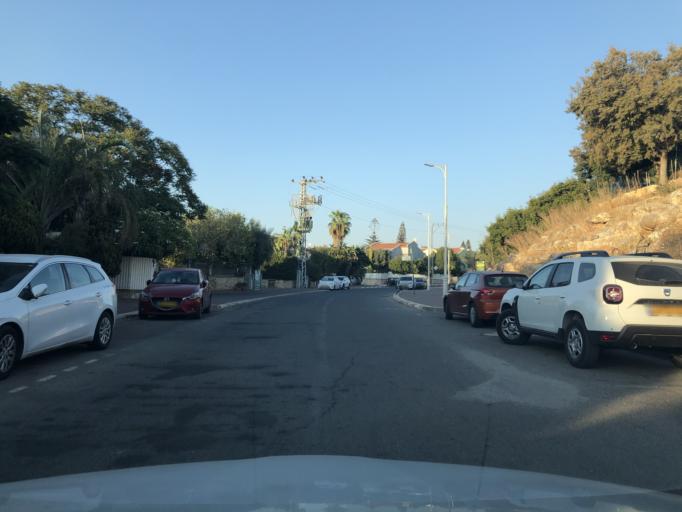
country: PS
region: West Bank
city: Hablah
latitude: 32.1594
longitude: 34.9704
